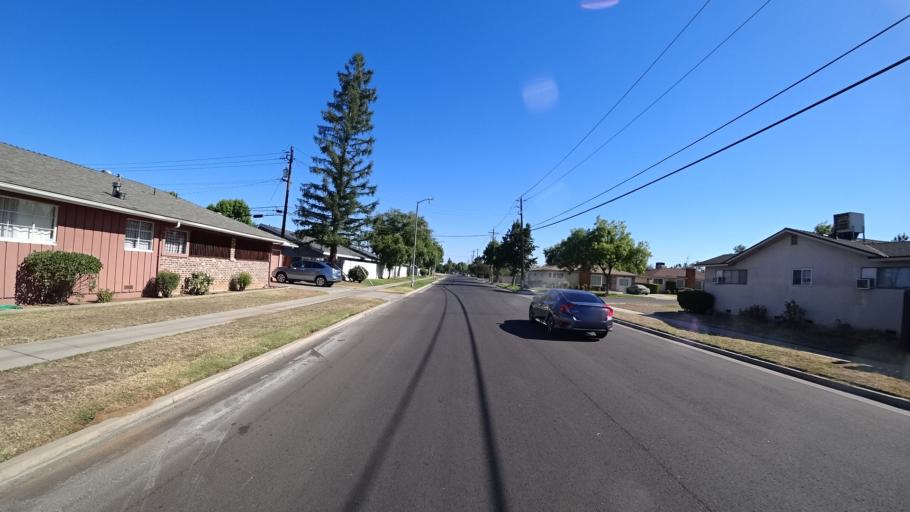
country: US
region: California
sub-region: Fresno County
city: Fresno
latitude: 36.7844
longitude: -119.8310
